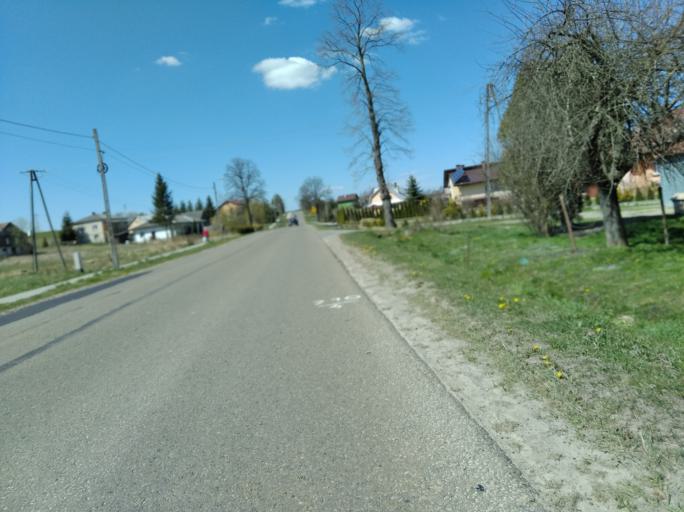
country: PL
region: Subcarpathian Voivodeship
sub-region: Powiat brzozowski
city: Dydnia
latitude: 49.6893
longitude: 22.1631
